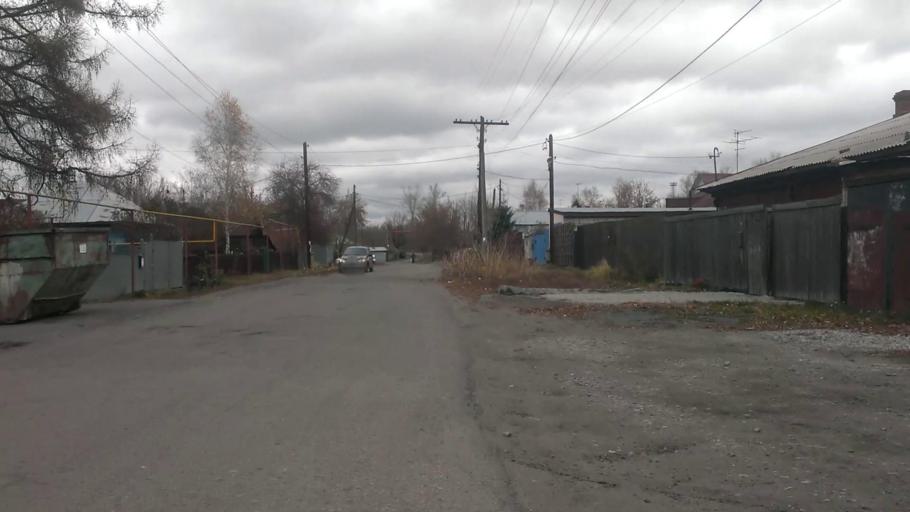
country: RU
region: Altai Krai
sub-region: Gorod Barnaulskiy
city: Barnaul
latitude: 53.3526
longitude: 83.7532
